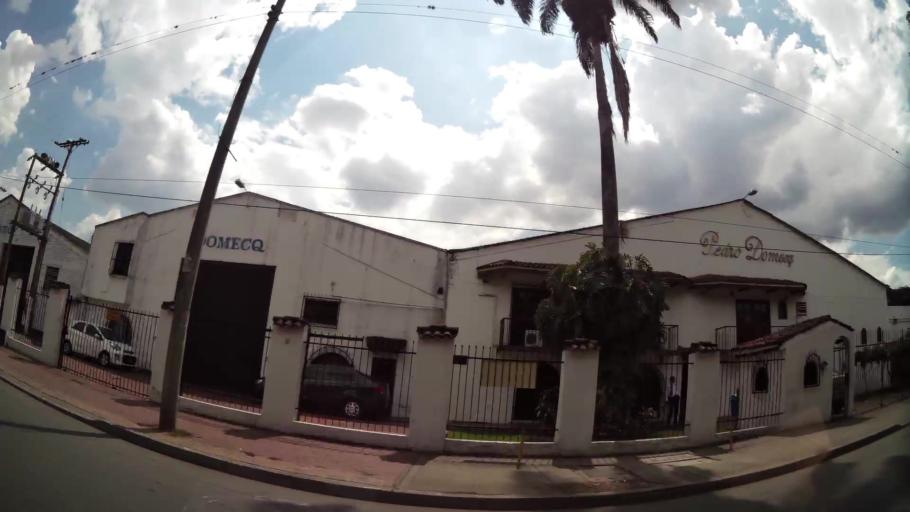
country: CO
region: Valle del Cauca
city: Cali
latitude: 3.4716
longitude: -76.5058
